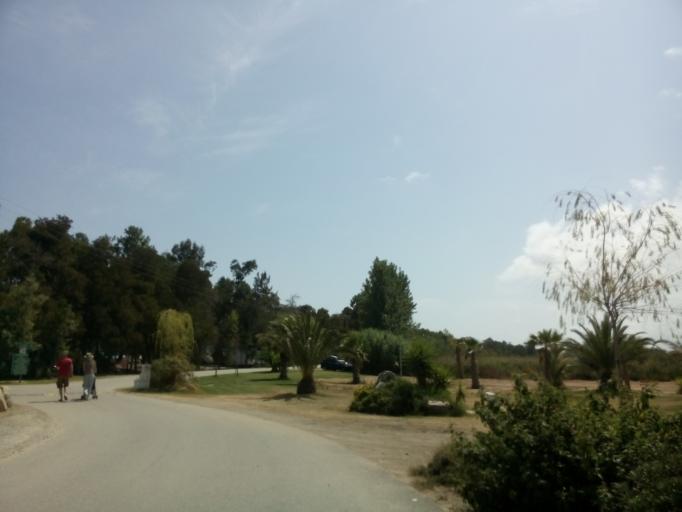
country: FR
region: Corsica
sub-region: Departement de la Haute-Corse
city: Aleria
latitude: 42.1112
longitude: 9.5493
